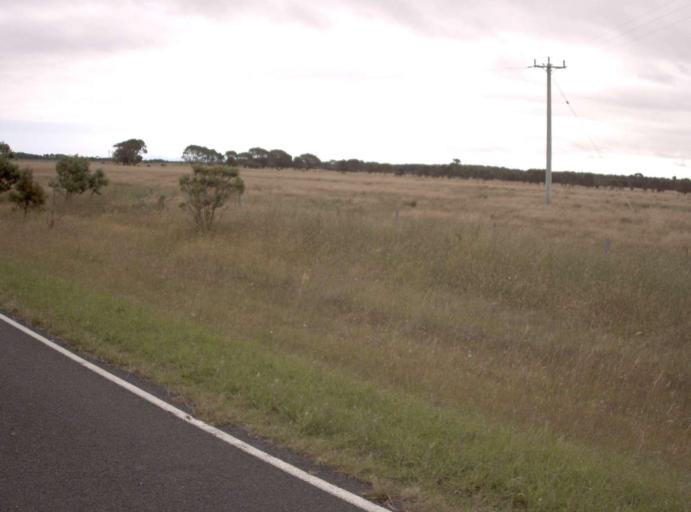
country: AU
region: Victoria
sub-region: Wellington
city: Sale
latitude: -38.5730
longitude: 146.8777
